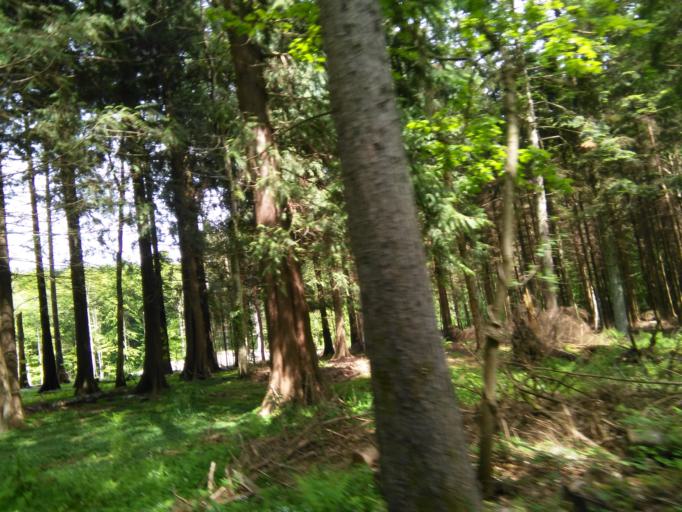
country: DK
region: Central Jutland
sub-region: Arhus Kommune
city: Beder
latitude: 56.0627
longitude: 10.2539
